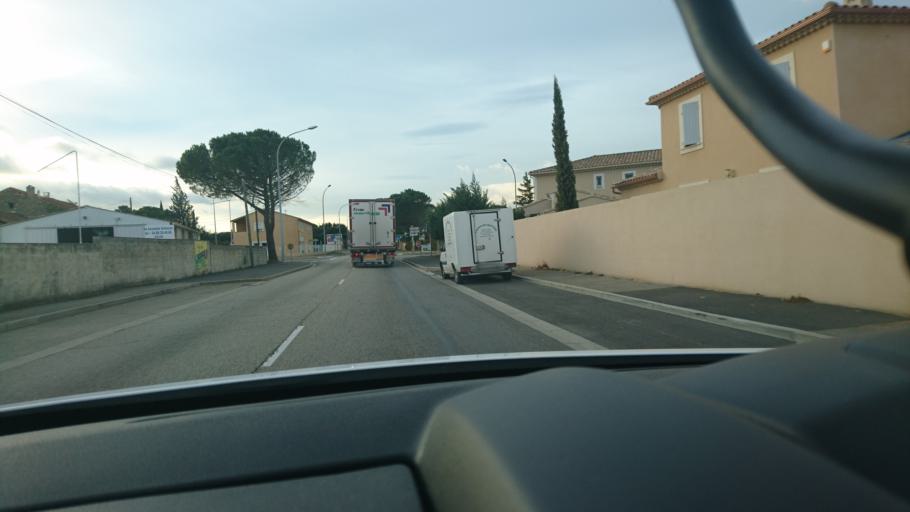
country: FR
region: Provence-Alpes-Cote d'Azur
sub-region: Departement du Vaucluse
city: Bollene
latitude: 44.2880
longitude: 4.7562
